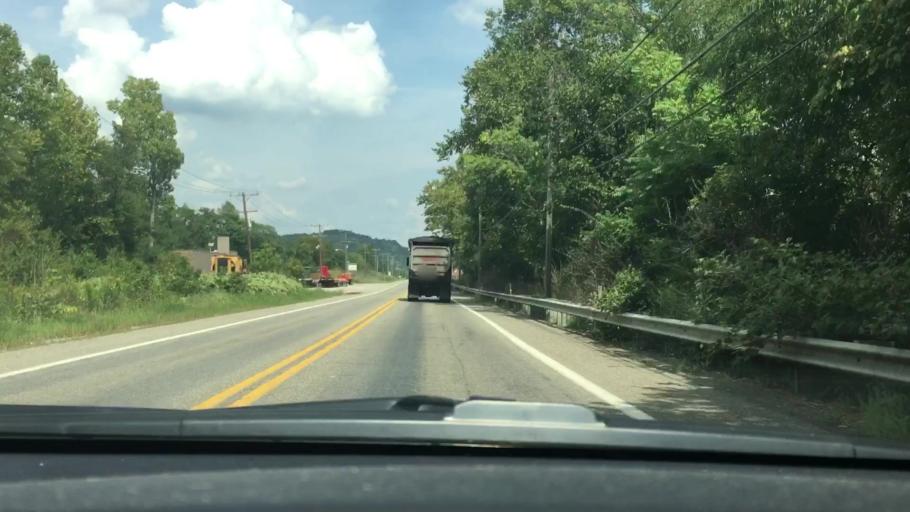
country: US
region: Pennsylvania
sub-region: Allegheny County
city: Elizabeth
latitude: 40.2599
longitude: -79.9140
